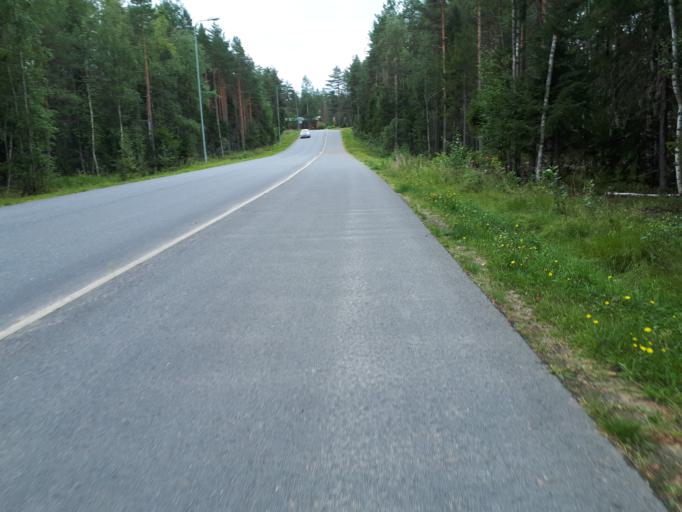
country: FI
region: Northern Ostrobothnia
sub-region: Oulunkaari
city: Ii
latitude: 65.3209
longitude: 25.4100
